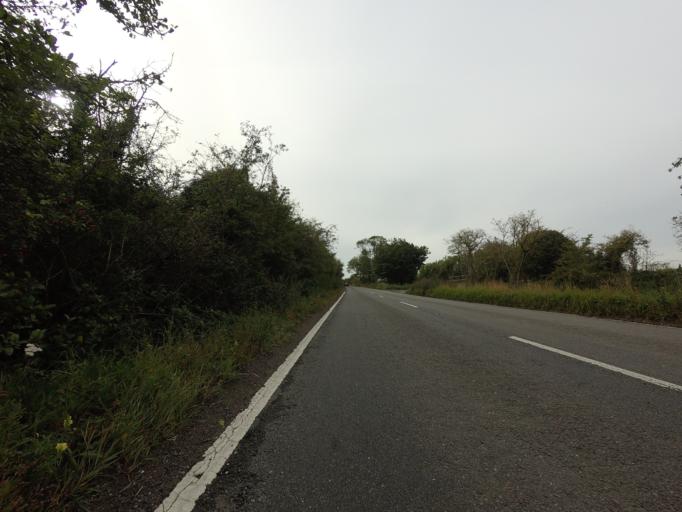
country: GB
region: England
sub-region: Cambridgeshire
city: Melbourn
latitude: 52.0378
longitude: 0.0419
